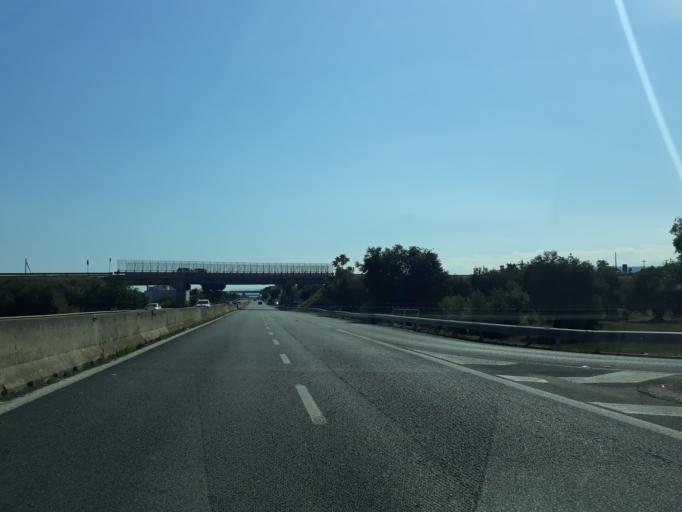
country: IT
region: Apulia
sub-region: Provincia di Bari
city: Monopoli
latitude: 40.8955
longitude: 17.3303
